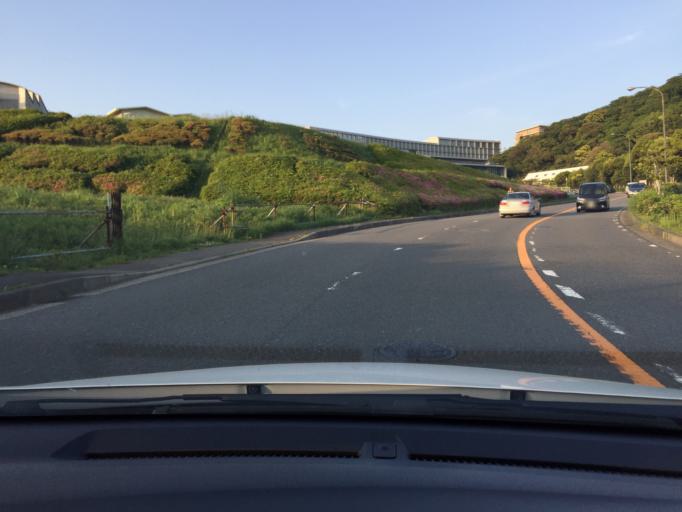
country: JP
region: Kanagawa
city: Hayama
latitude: 35.2529
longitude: 139.6066
